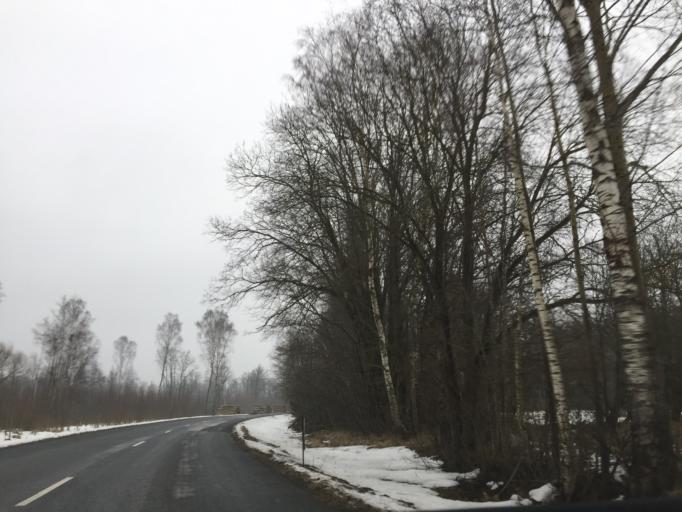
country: EE
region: Saare
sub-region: Kuressaare linn
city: Kuressaare
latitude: 58.3450
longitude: 22.7921
